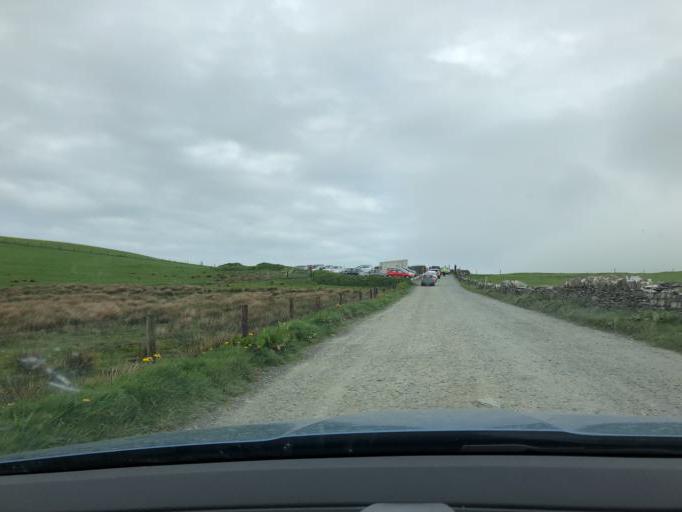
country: IE
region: Munster
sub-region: An Clar
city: Kilrush
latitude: 52.9628
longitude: -9.4314
